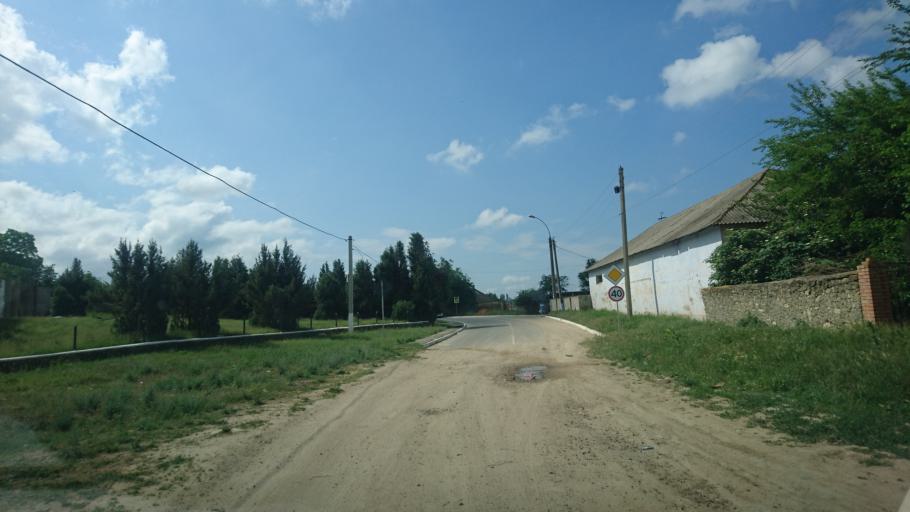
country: MD
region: Telenesti
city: Cocieri
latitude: 47.3570
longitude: 29.1061
